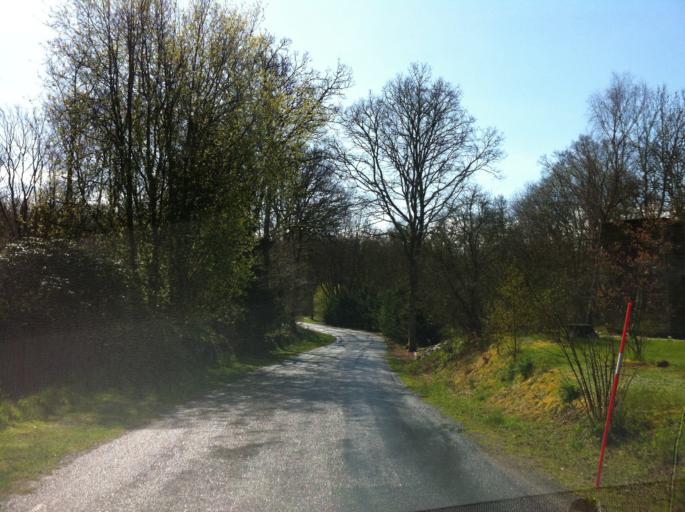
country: SE
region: Skane
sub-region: Hoors Kommun
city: Satofta
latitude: 55.9134
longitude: 13.6113
